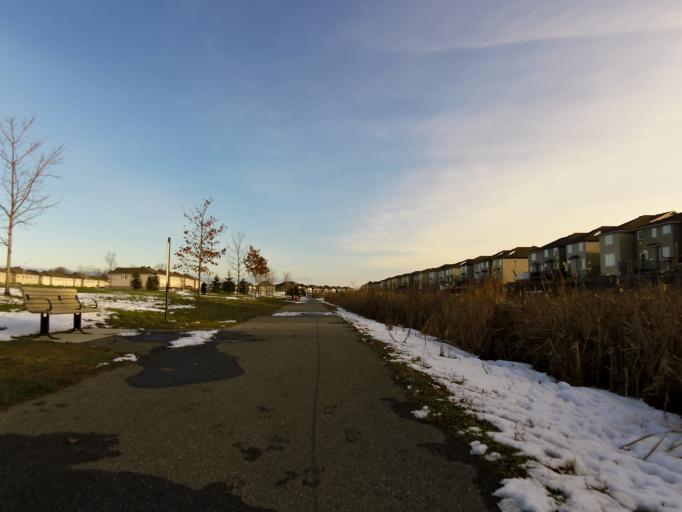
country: CA
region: Ontario
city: Bells Corners
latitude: 45.2810
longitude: -75.8723
